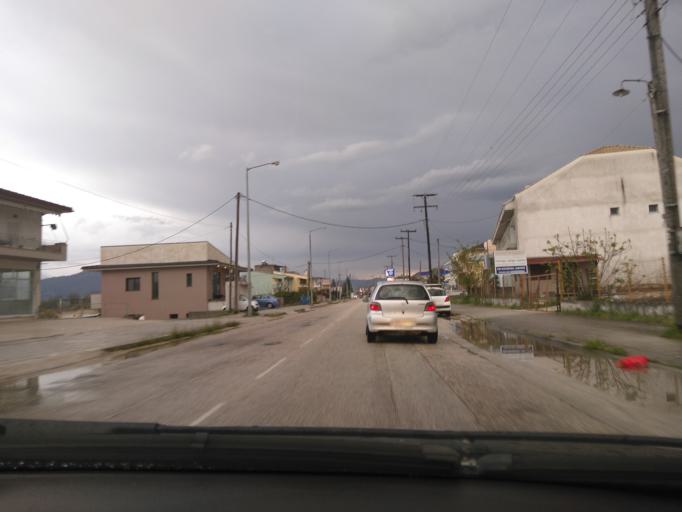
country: GR
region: Epirus
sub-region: Nomos Ioanninon
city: Anatoli
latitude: 39.6354
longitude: 20.8724
